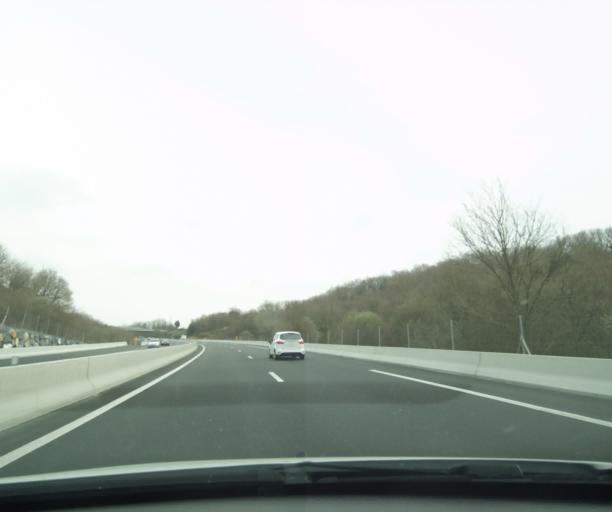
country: FR
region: Aquitaine
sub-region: Departement des Pyrenees-Atlantiques
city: Mouguerre
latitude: 43.4581
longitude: -1.4192
